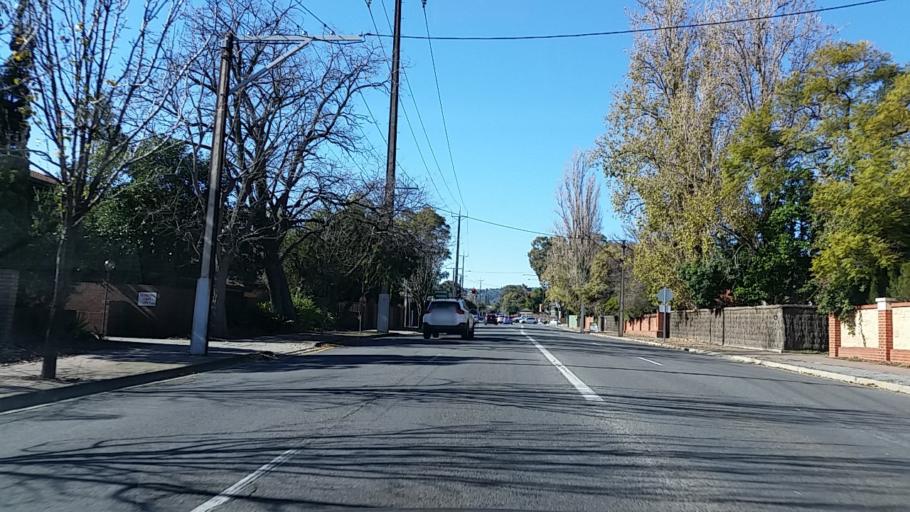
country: AU
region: South Australia
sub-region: Norwood Payneham St Peters
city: Trinity Gardens
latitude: -34.9271
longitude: 138.6396
